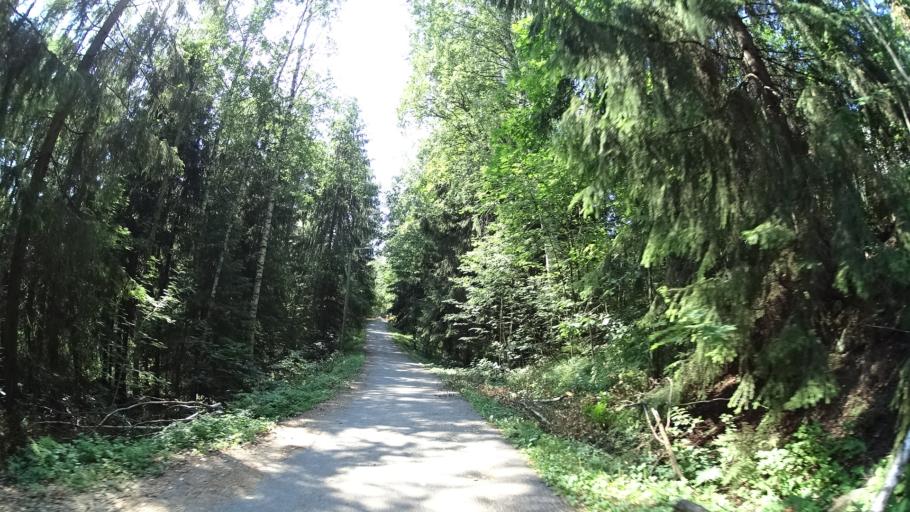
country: FI
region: Uusimaa
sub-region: Helsinki
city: Vantaa
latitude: 60.3448
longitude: 25.0705
